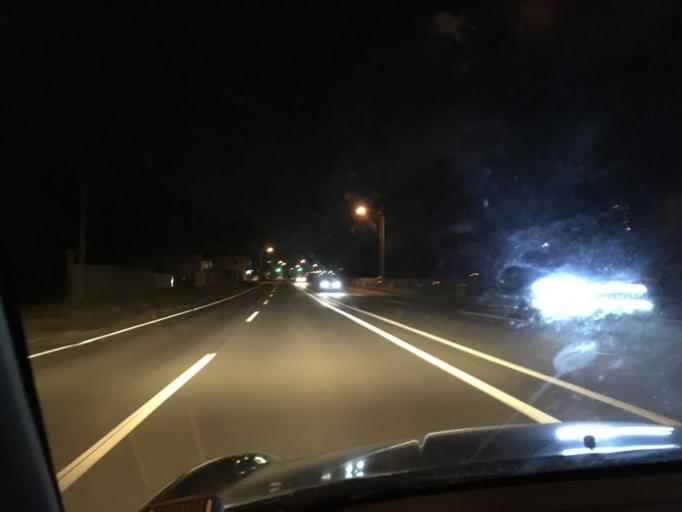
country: JP
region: Hokkaido
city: Muroran
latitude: 42.3549
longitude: 140.9894
